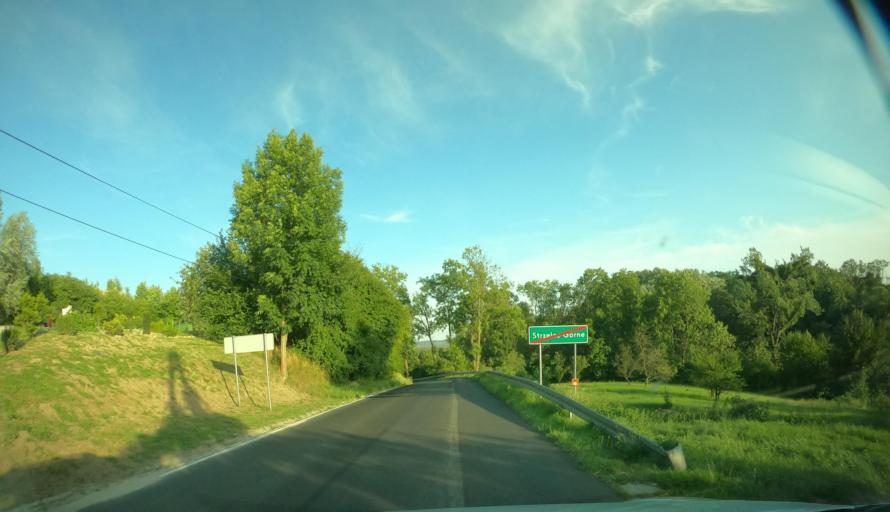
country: PL
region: Kujawsko-Pomorskie
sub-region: Bydgoszcz
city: Fordon
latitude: 53.2094
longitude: 18.1695
